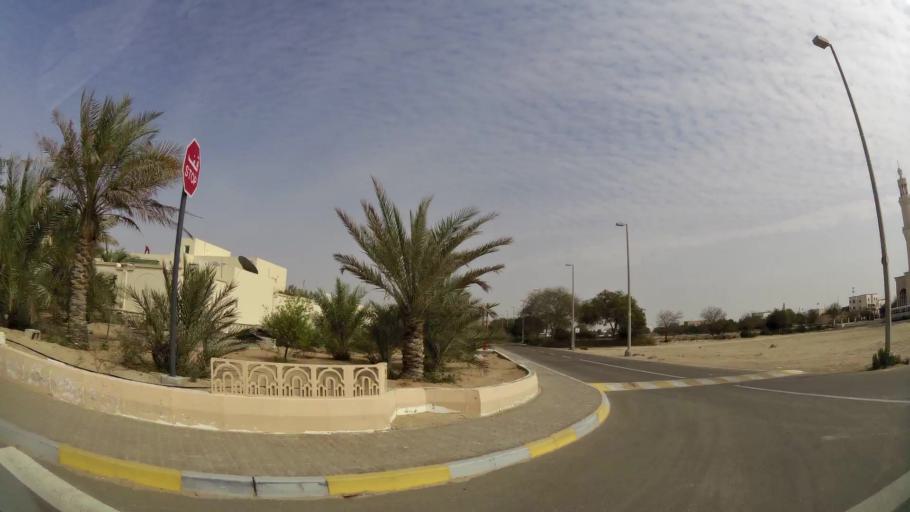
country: AE
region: Abu Dhabi
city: Abu Dhabi
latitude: 24.5772
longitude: 54.6872
